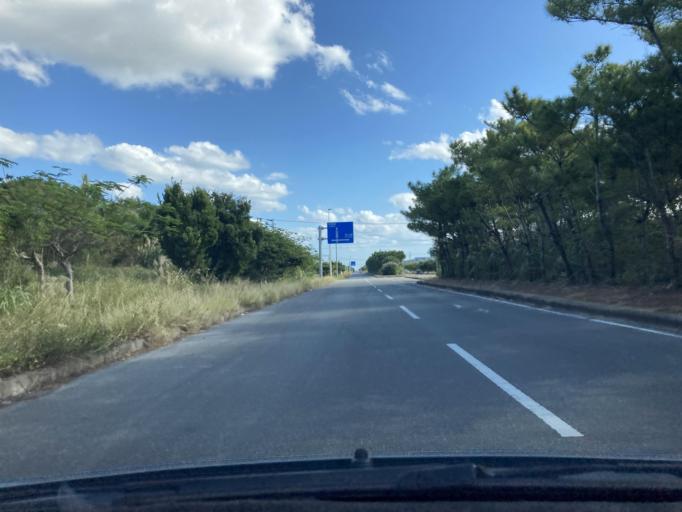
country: JP
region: Okinawa
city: Katsuren-haebaru
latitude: 26.3383
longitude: 127.8612
